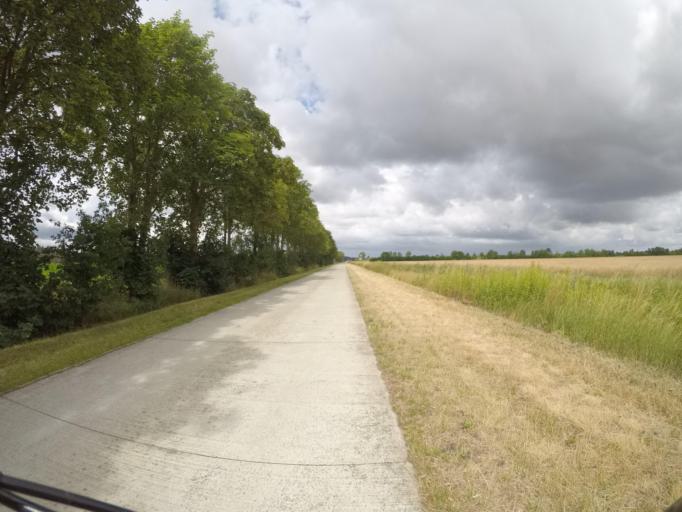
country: DE
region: Lower Saxony
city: Hitzacker
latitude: 53.1967
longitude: 11.1113
